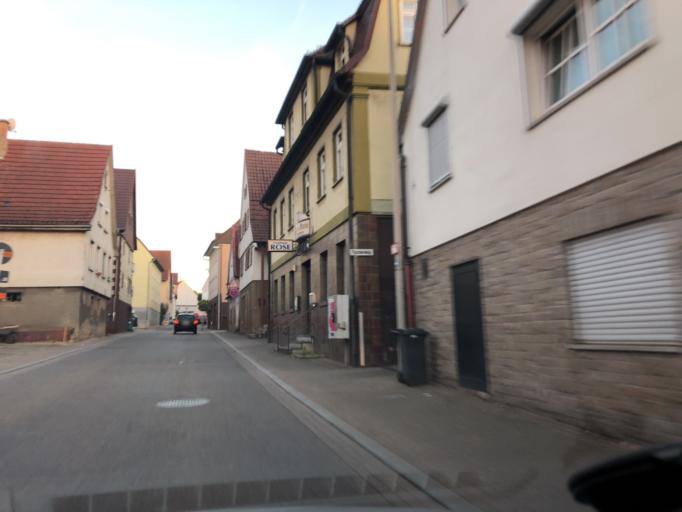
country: DE
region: Baden-Wuerttemberg
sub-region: Regierungsbezirk Stuttgart
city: Erdmannhausen
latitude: 48.8883
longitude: 9.2765
